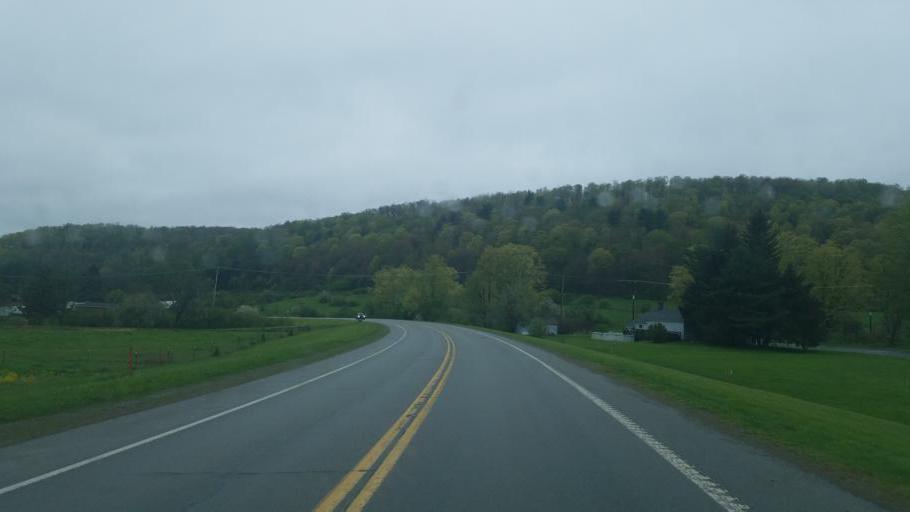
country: US
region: Pennsylvania
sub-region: Potter County
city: Coudersport
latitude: 41.8108
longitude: -78.0166
